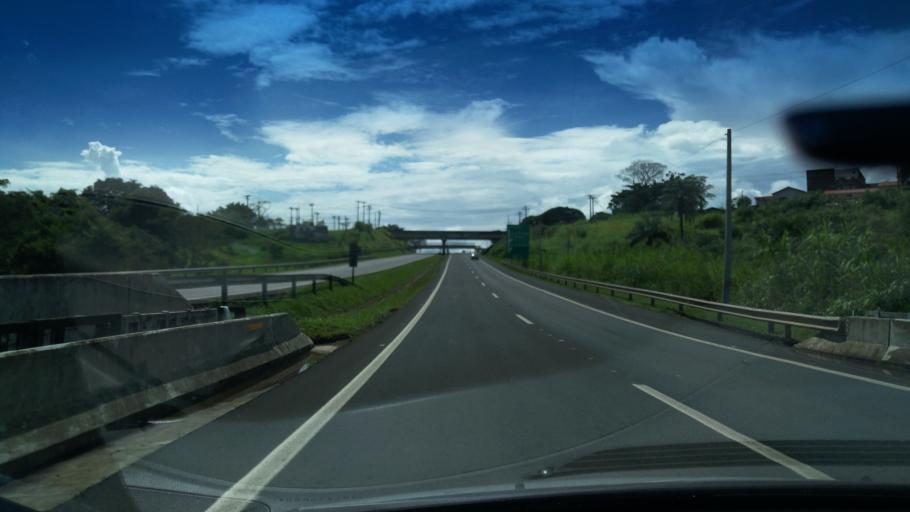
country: BR
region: Sao Paulo
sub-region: Santo Antonio Do Jardim
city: Espirito Santo do Pinhal
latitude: -22.1955
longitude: -46.7739
